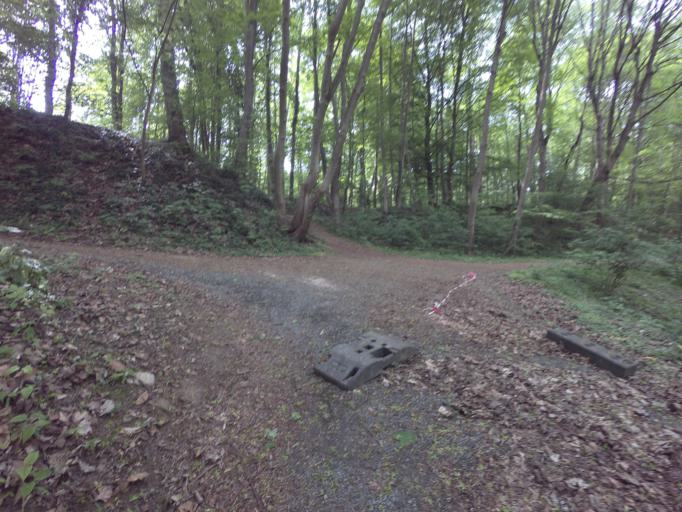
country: DE
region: Lower Saxony
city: Nordstemmen
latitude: 52.1730
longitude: 9.7682
